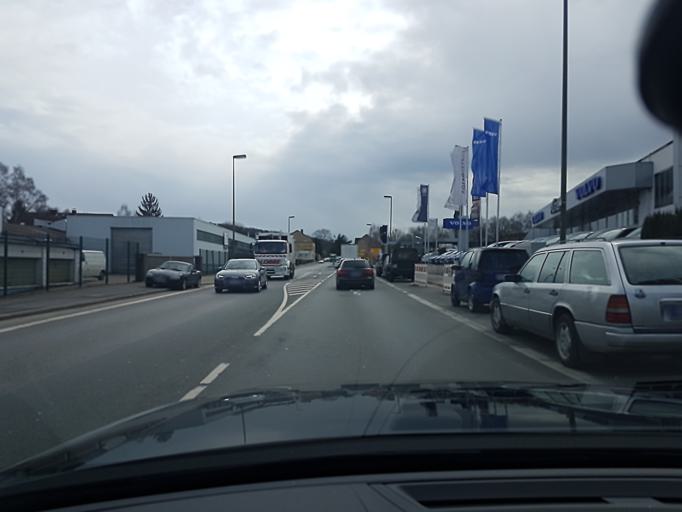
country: DE
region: North Rhine-Westphalia
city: Iserlohn
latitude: 51.4053
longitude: 7.6961
